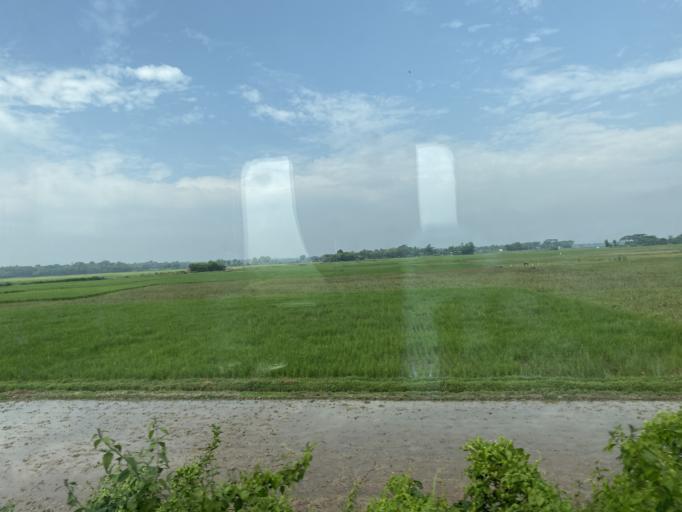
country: IN
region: Tripura
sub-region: West Tripura
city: Agartala
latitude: 23.9929
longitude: 91.2863
